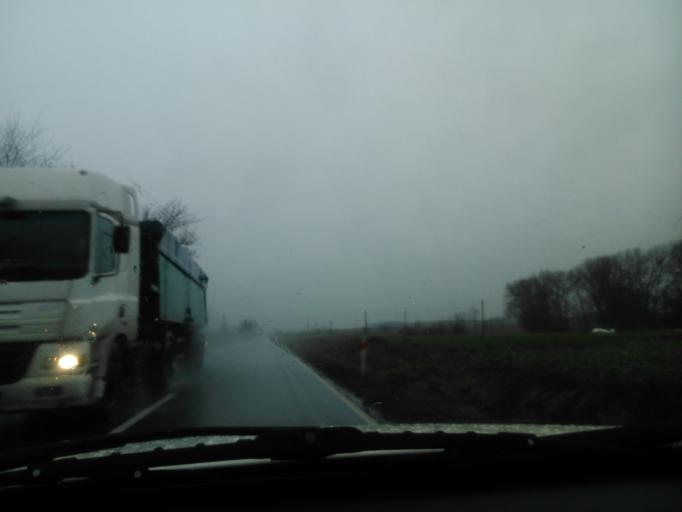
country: PL
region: Kujawsko-Pomorskie
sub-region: Powiat golubsko-dobrzynski
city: Radomin
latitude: 53.0790
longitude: 19.2288
